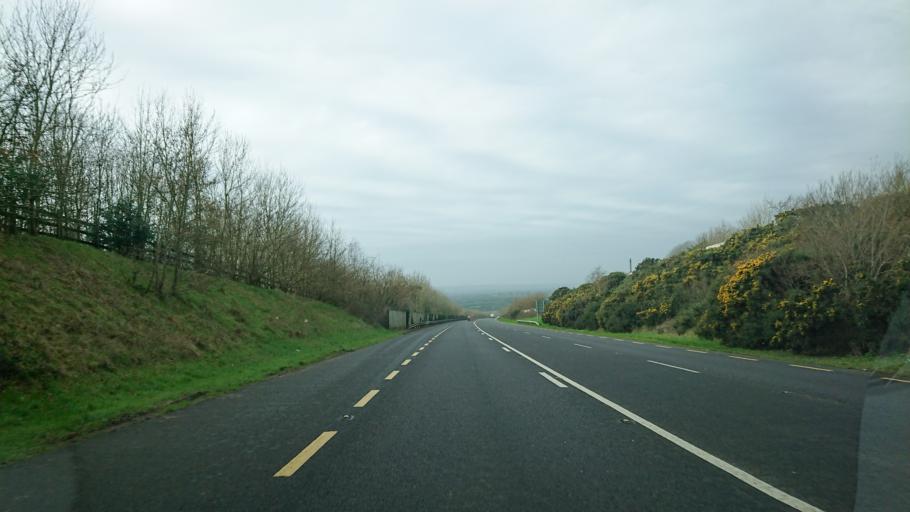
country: IE
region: Munster
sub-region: County Cork
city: Youghal
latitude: 51.9463
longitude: -7.8857
